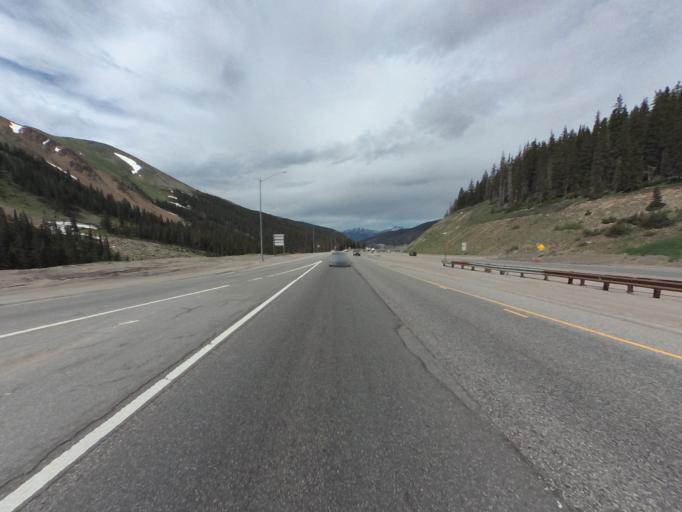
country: US
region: Colorado
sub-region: Summit County
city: Keystone
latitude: 39.6773
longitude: -105.9394
